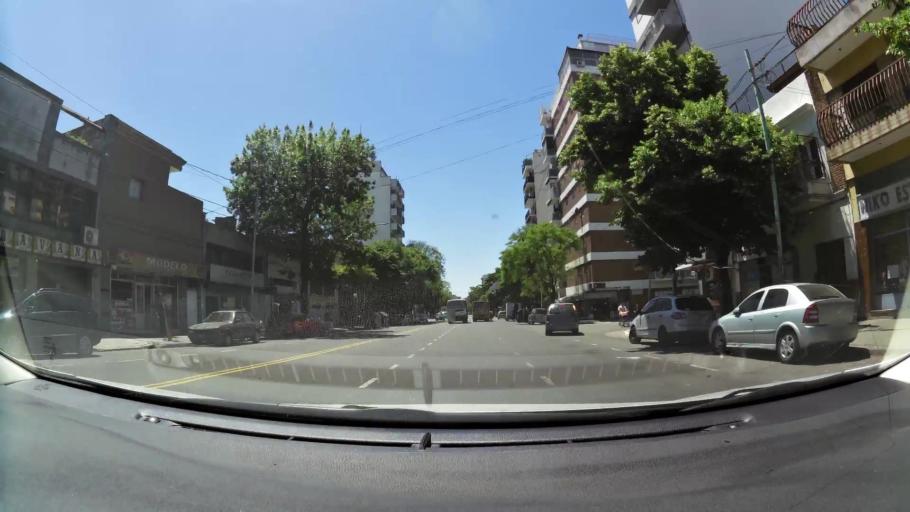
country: AR
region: Buenos Aires F.D.
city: Buenos Aires
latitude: -34.6340
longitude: -58.3897
